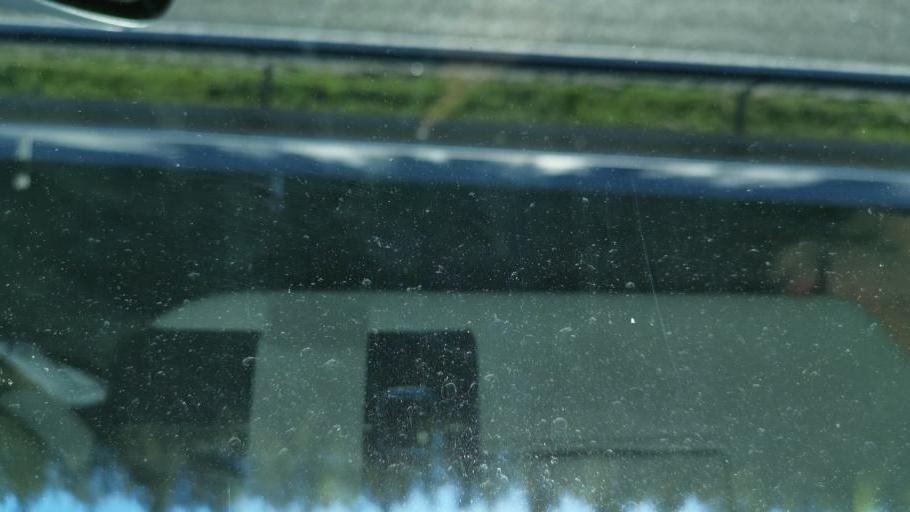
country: SE
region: Vaestra Goetaland
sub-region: Uddevalla Kommun
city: Ljungskile
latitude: 58.1742
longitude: 11.9009
